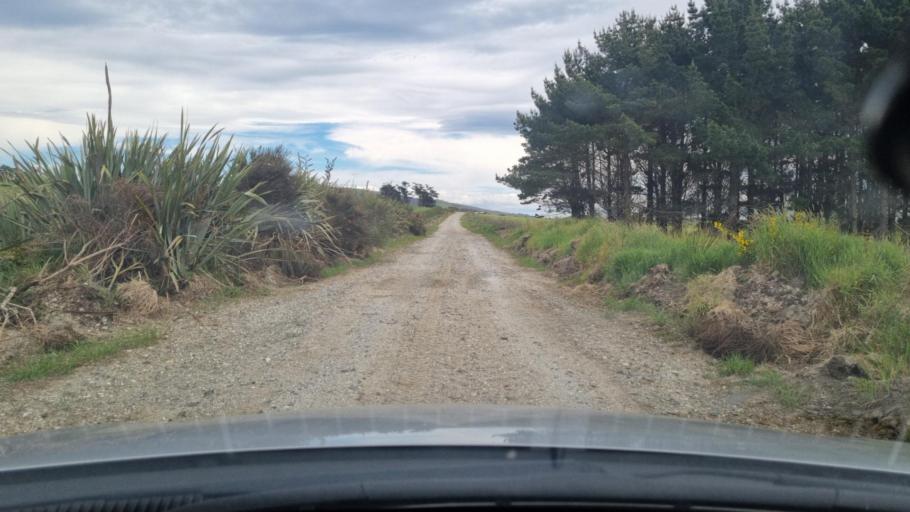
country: NZ
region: Southland
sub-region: Invercargill City
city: Bluff
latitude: -46.5202
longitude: 168.2993
